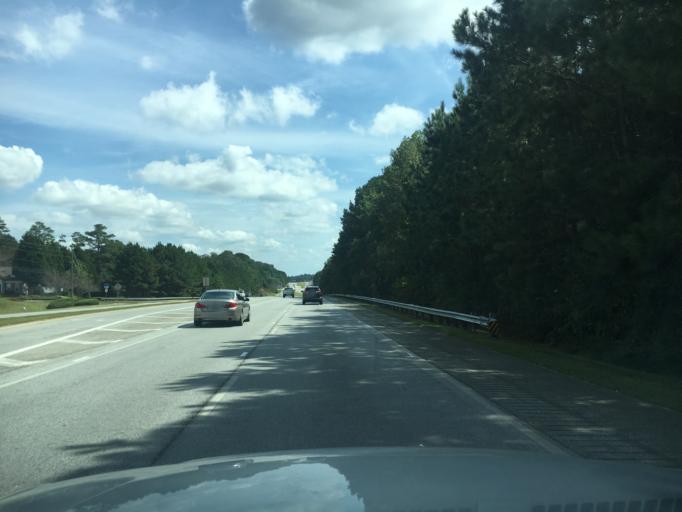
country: US
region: Georgia
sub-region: Gwinnett County
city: Duluth
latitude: 34.0224
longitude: -84.1357
